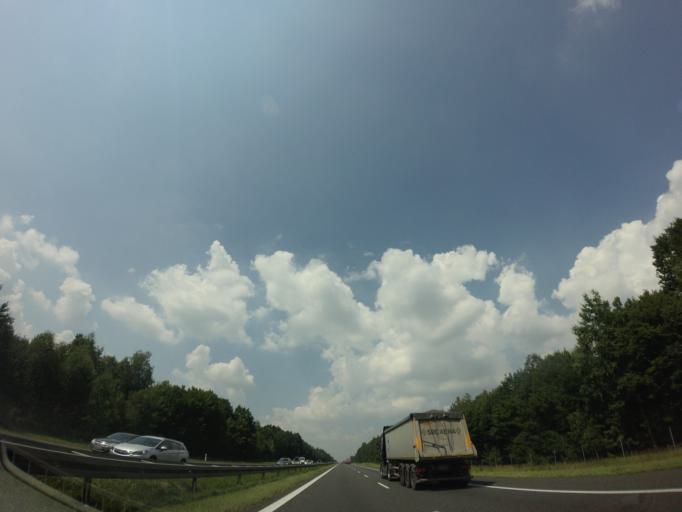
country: PL
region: Silesian Voivodeship
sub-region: Powiat gliwicki
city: Toszek
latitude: 50.3668
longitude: 18.5029
